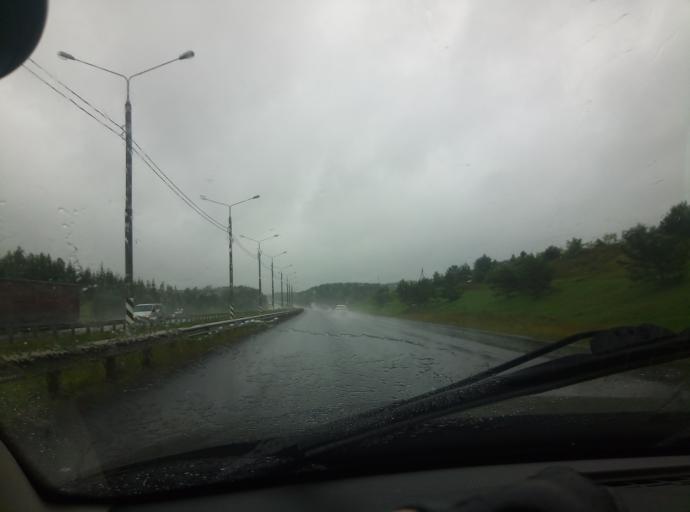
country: RU
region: Tula
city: Zaokskiy
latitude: 54.7704
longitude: 37.4888
